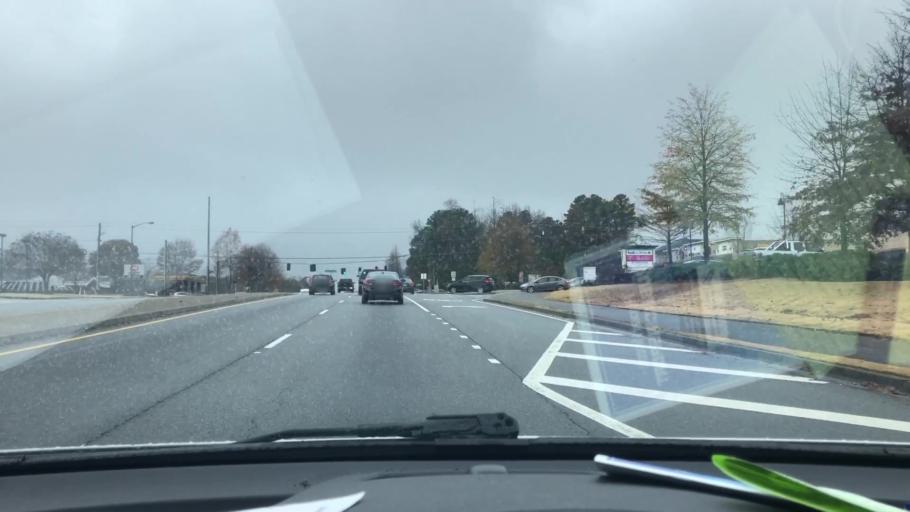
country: US
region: Georgia
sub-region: Gwinnett County
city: Berkeley Lake
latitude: 33.9684
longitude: -84.1934
